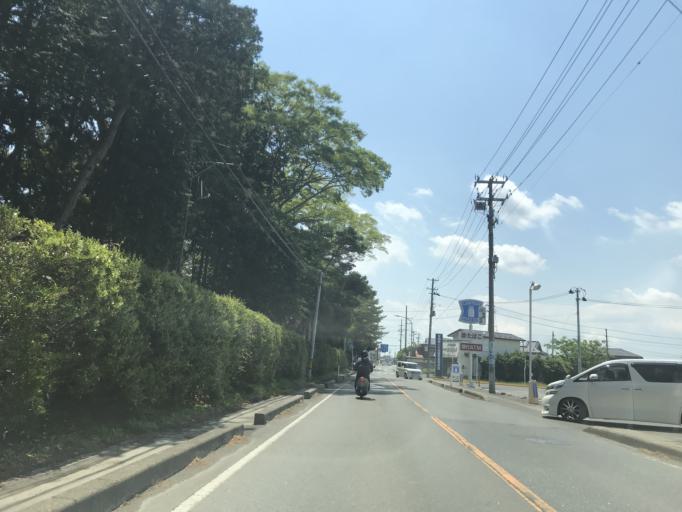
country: JP
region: Miyagi
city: Kogota
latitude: 38.5558
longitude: 141.0590
